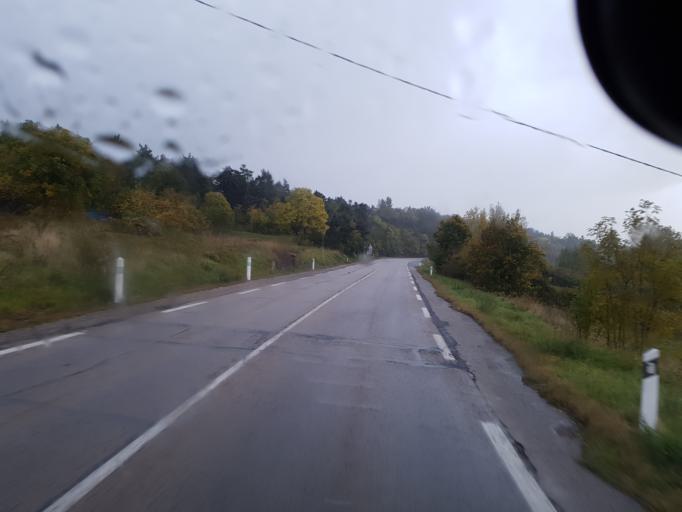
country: FR
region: Auvergne
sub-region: Departement de la Haute-Loire
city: Cussac-sur-Loire
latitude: 45.0054
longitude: 3.8793
